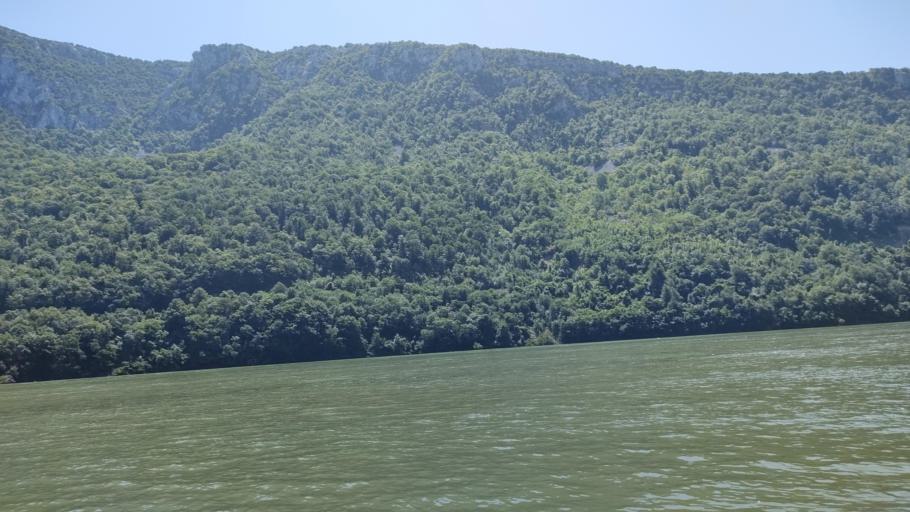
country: RO
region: Mehedinti
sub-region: Comuna Dubova
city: Dubova
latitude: 44.5931
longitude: 22.2611
